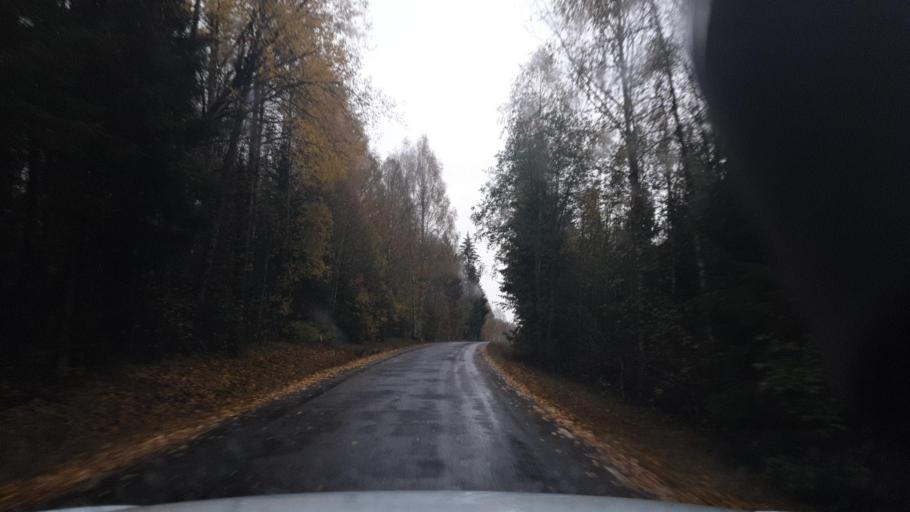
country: SE
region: Vaermland
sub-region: Eda Kommun
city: Amotfors
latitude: 59.8377
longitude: 12.4318
